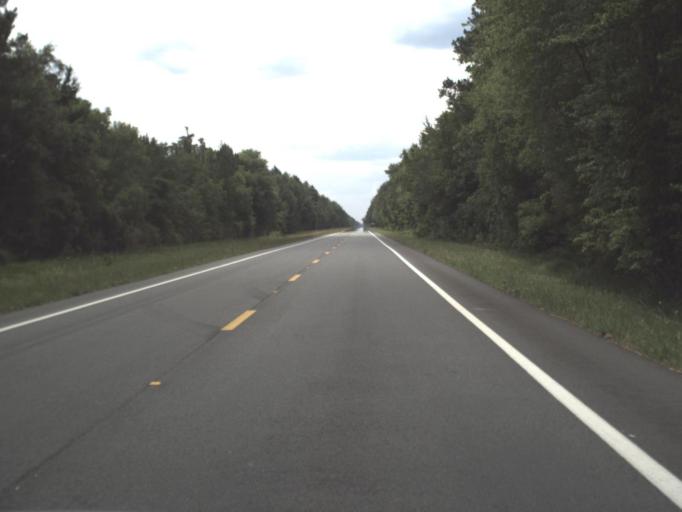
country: US
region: Florida
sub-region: Columbia County
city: Five Points
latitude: 30.4731
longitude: -82.6563
